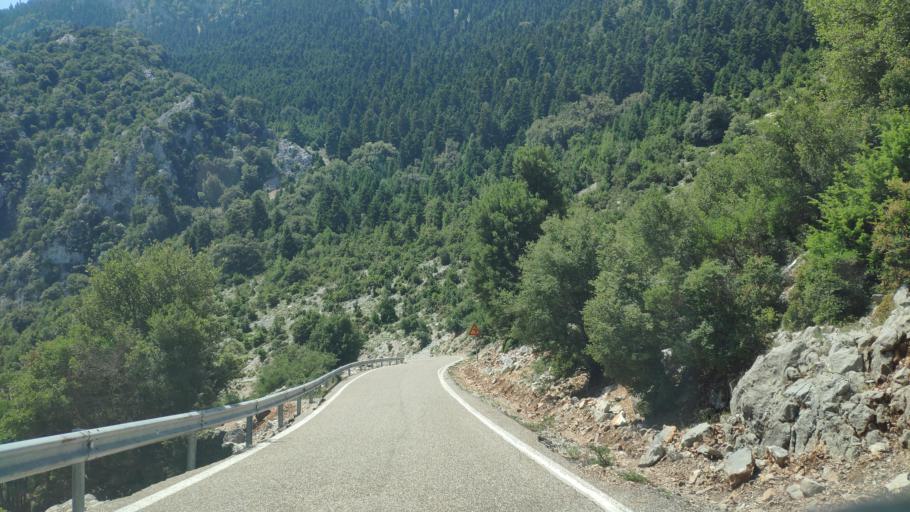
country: GR
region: West Greece
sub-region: Nomos Aitolias kai Akarnanias
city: Krikellos
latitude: 39.0093
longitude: 21.3605
